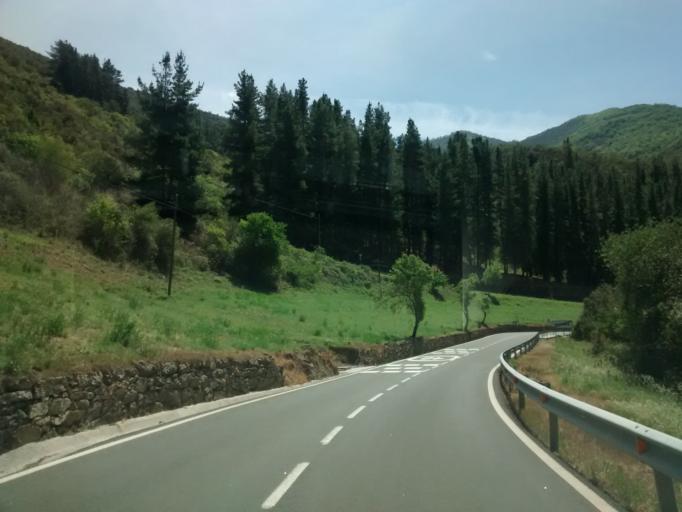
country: ES
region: Cantabria
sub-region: Provincia de Cantabria
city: Potes
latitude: 43.1208
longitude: -4.6288
